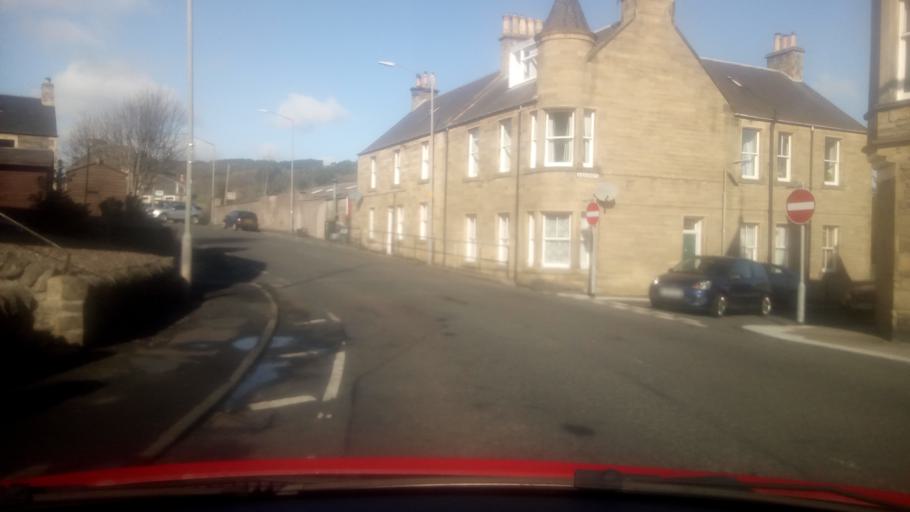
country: GB
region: Scotland
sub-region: The Scottish Borders
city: Selkirk
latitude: 55.5475
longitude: -2.8479
